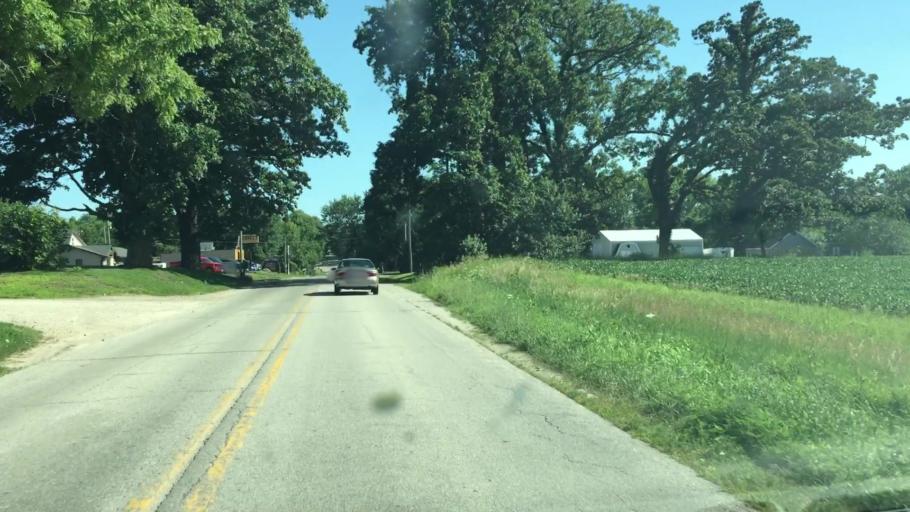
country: US
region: Iowa
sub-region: Linn County
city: Ely
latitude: 41.8519
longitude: -91.6462
